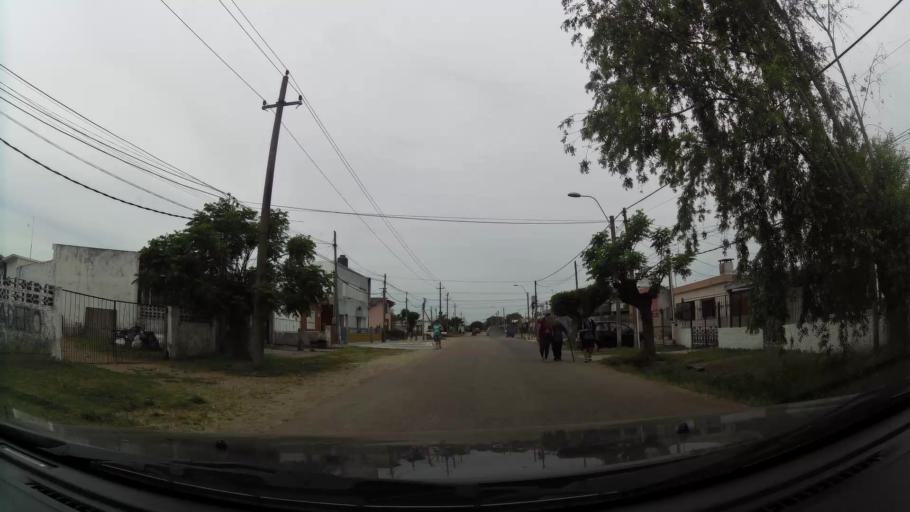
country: UY
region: Canelones
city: Las Piedras
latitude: -34.7395
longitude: -56.2284
